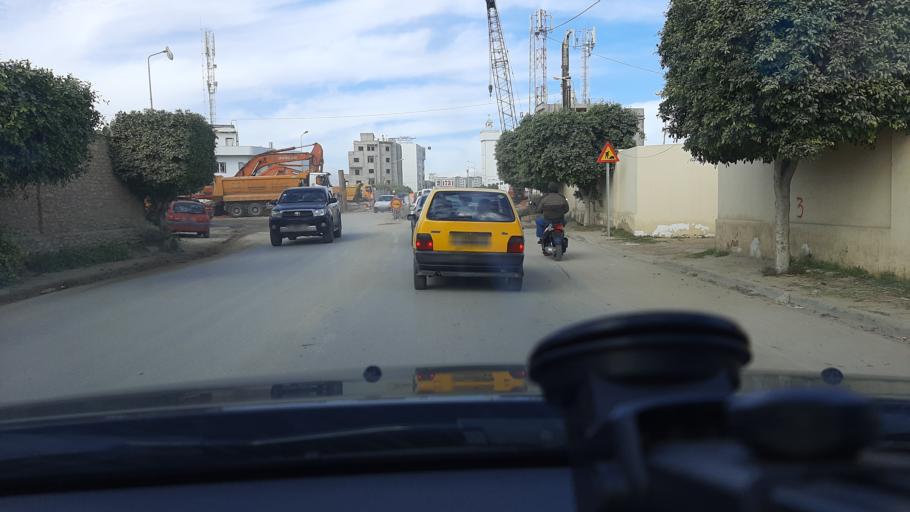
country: TN
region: Safaqis
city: Sfax
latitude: 34.7563
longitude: 10.7353
